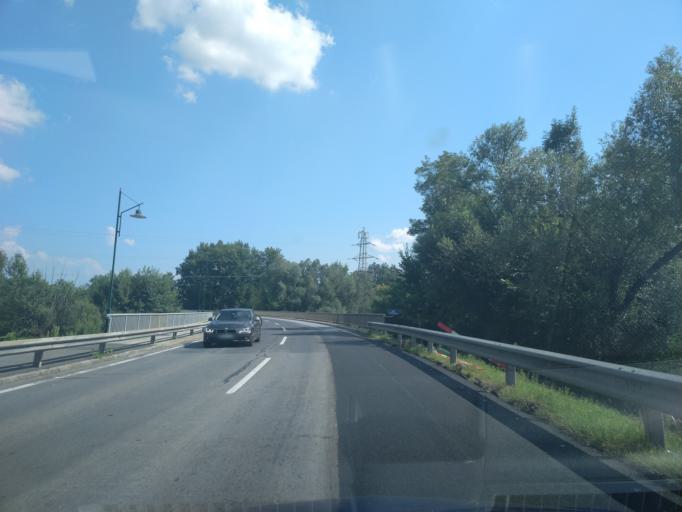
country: AT
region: Styria
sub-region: Politischer Bezirk Leibnitz
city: Gabersdorf
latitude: 46.7669
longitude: 15.5711
